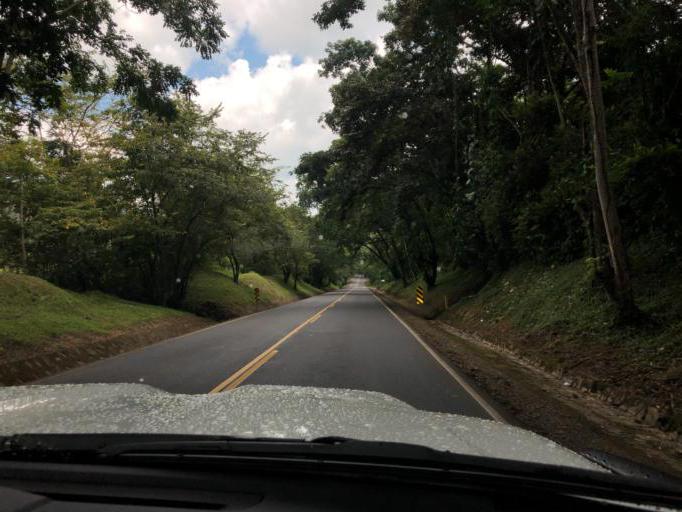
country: NI
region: Chontales
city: Villa Sandino
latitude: 11.9964
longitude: -84.9185
